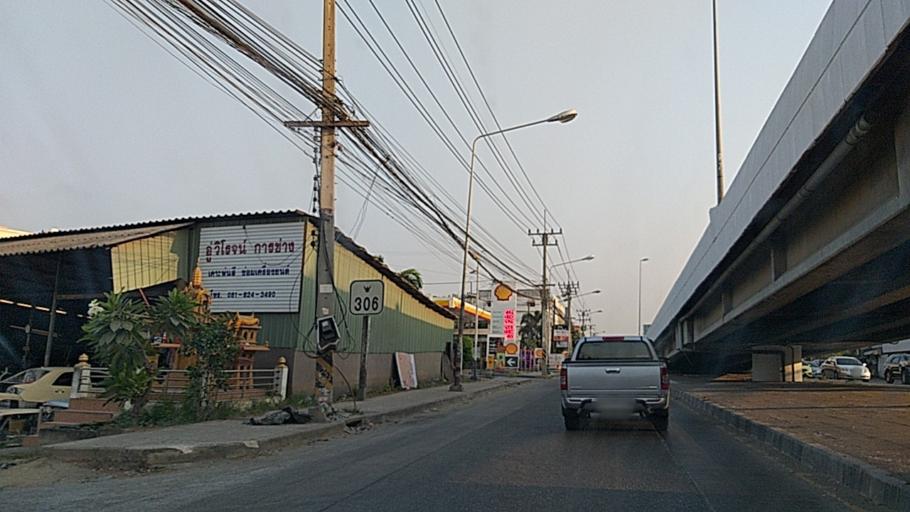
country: TH
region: Phra Nakhon Si Ayutthaya
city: Ban Bang Kadi Pathum Thani
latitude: 14.0031
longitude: 100.5551
